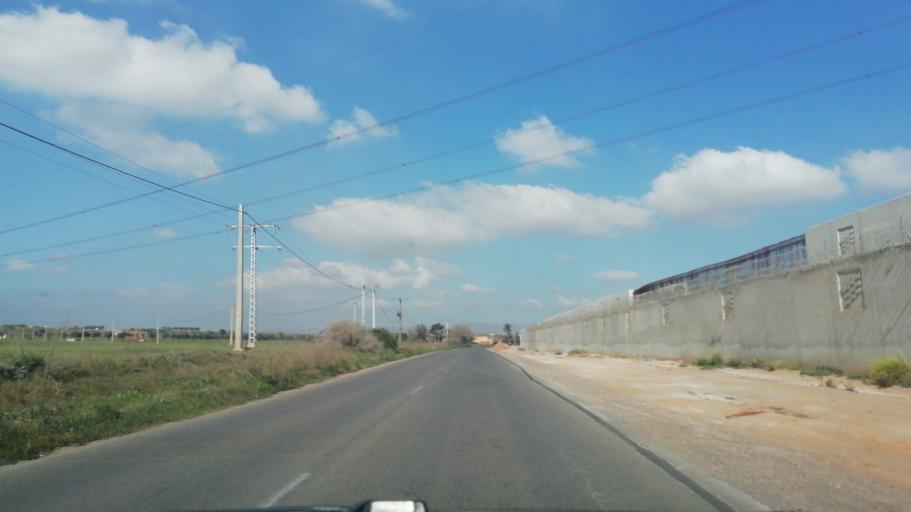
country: DZ
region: Oran
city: Ain el Bya
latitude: 35.7542
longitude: -0.2701
